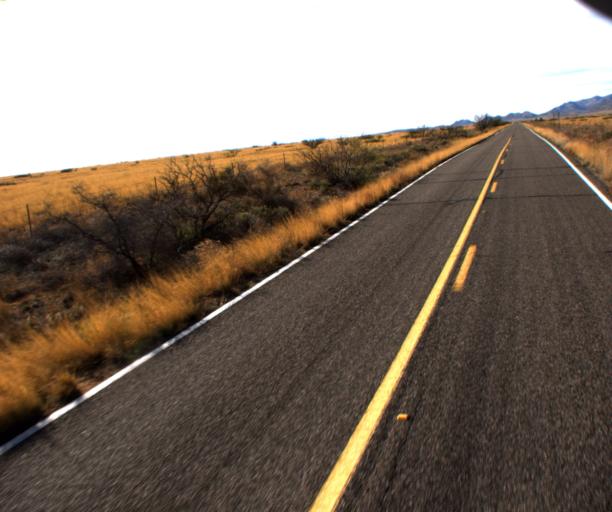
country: US
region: Arizona
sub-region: Cochise County
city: Willcox
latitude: 32.0846
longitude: -109.5253
